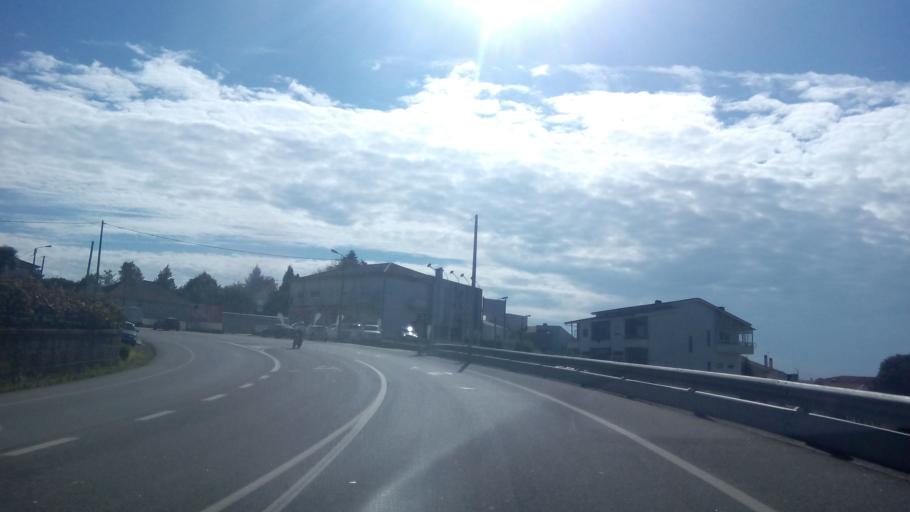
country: PT
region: Porto
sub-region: Paredes
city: Gandra
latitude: 41.1929
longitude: -8.4073
